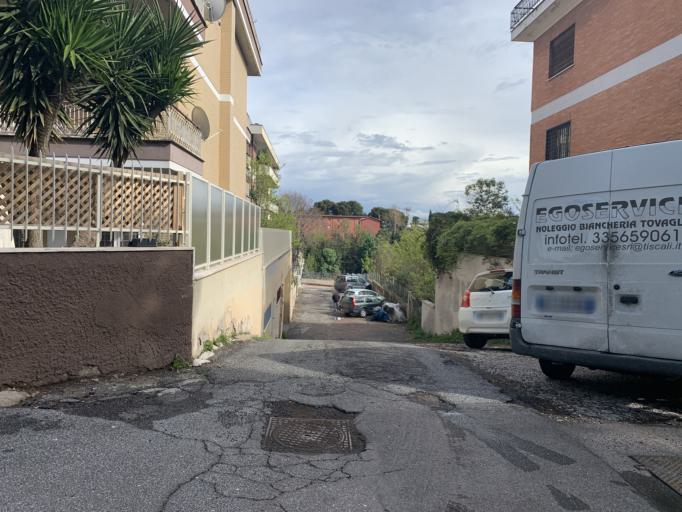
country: VA
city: Vatican City
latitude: 41.8784
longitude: 12.4179
